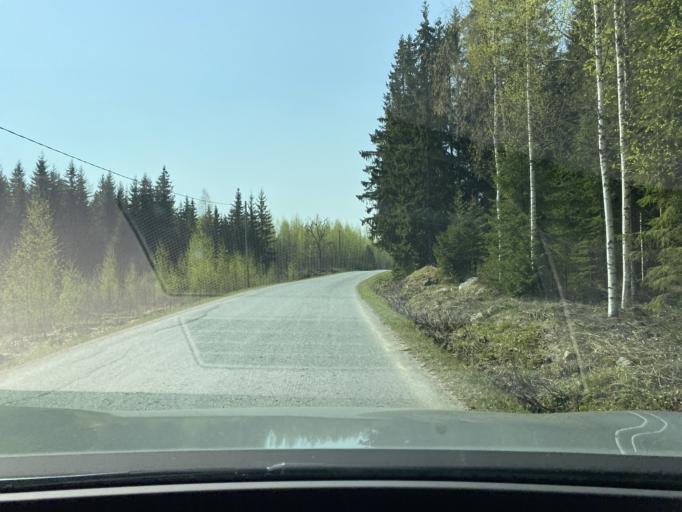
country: FI
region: Satakunta
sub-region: Pori
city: Huittinen
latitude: 61.1268
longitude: 22.8113
